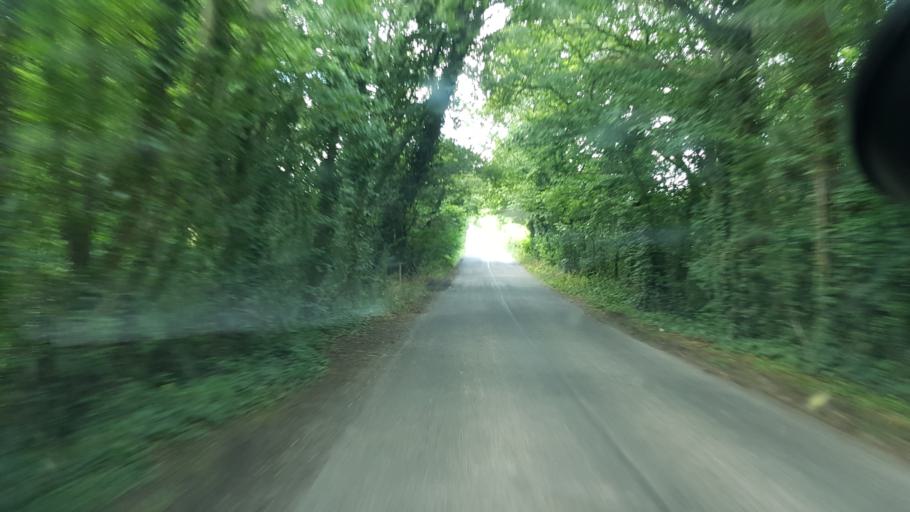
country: GB
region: England
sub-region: West Sussex
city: Billingshurst
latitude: 51.0304
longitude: -0.4342
